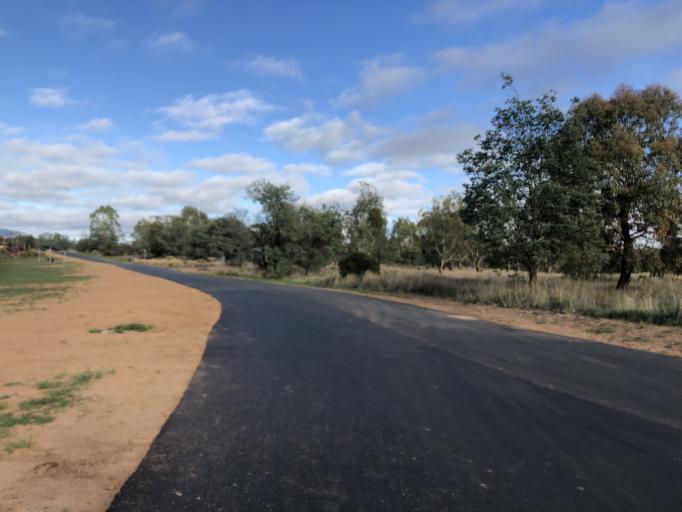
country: AU
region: New South Wales
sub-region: Orange Municipality
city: Orange
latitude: -33.3258
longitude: 149.0914
